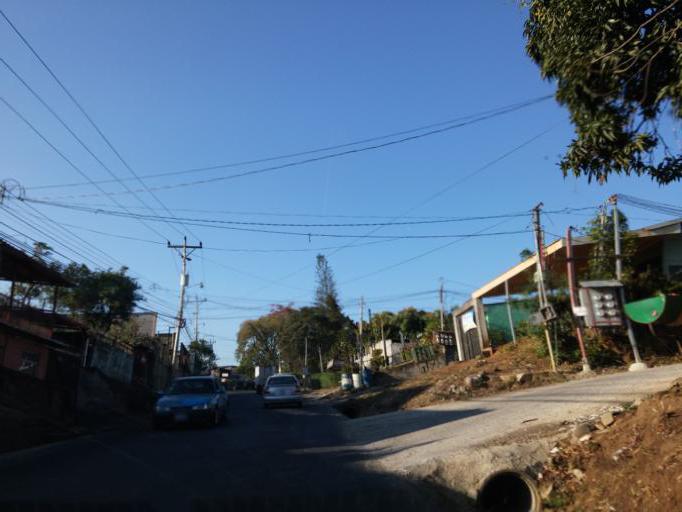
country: CR
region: Alajuela
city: Alajuela
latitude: 9.9782
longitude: -84.2252
